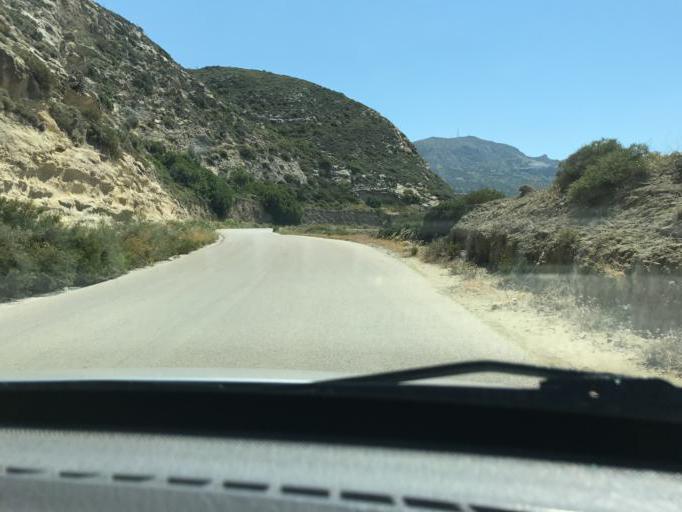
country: GR
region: South Aegean
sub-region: Nomos Dodekanisou
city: Karpathos
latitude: 35.5004
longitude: 27.1950
